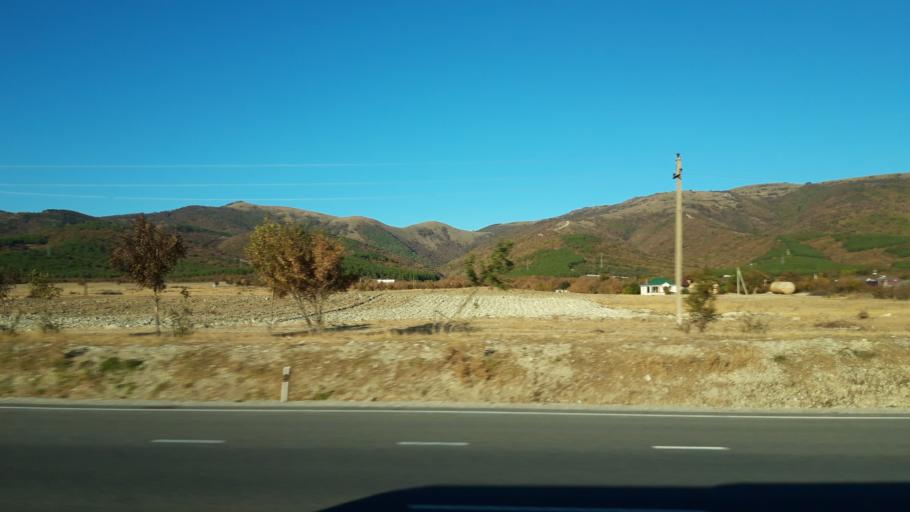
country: RU
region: Krasnodarskiy
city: Kabardinka
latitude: 44.6352
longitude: 37.9947
